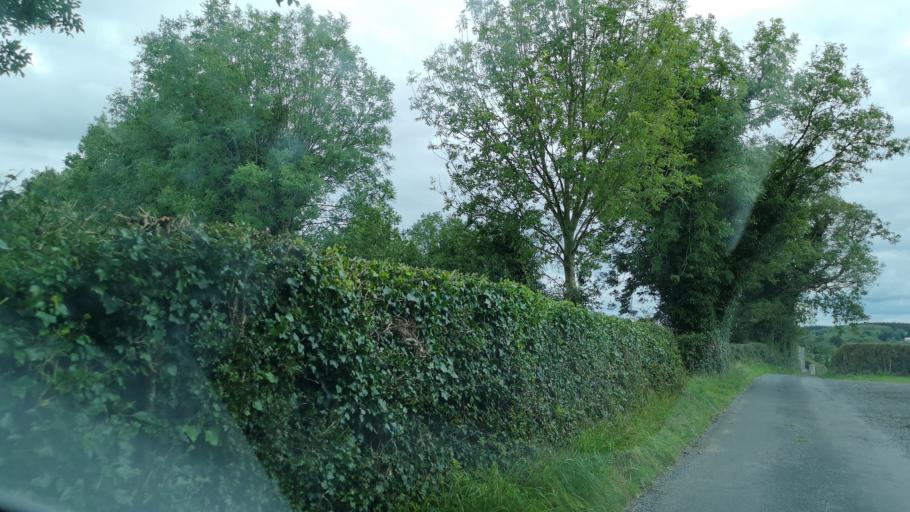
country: IE
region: Connaught
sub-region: County Galway
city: Loughrea
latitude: 53.1579
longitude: -8.4703
